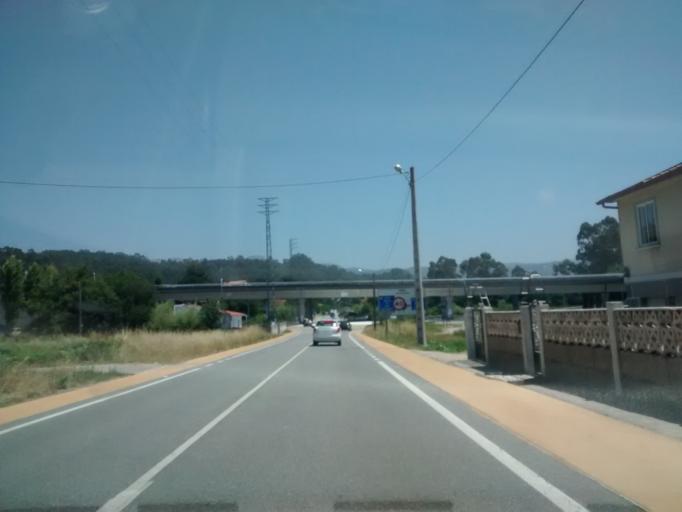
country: ES
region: Galicia
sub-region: Provincia de Pontevedra
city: Nigran
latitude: 42.1139
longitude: -8.7914
